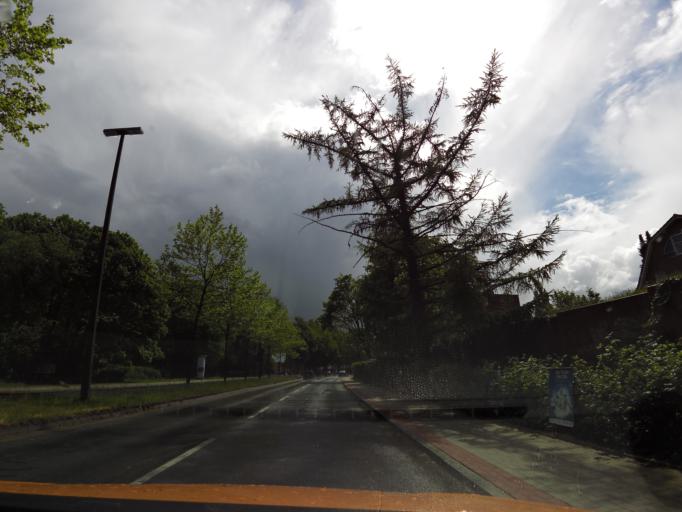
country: DE
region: Lower Saxony
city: Delmenhorst
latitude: 53.0459
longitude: 8.6373
